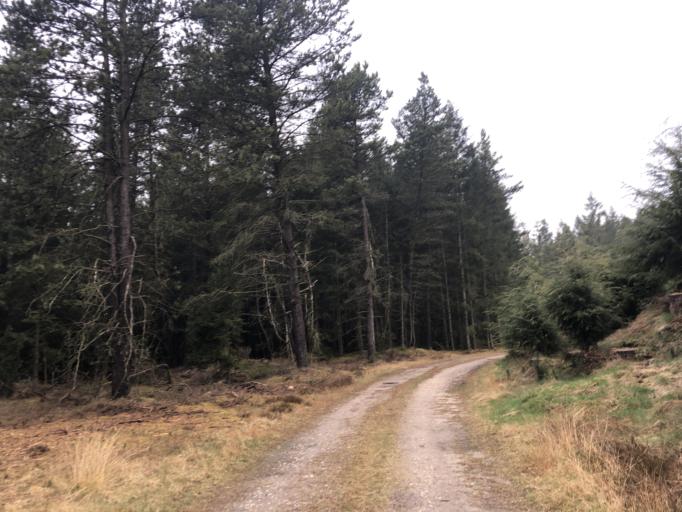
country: DK
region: Central Jutland
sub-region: Holstebro Kommune
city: Ulfborg
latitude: 56.2323
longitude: 8.4119
